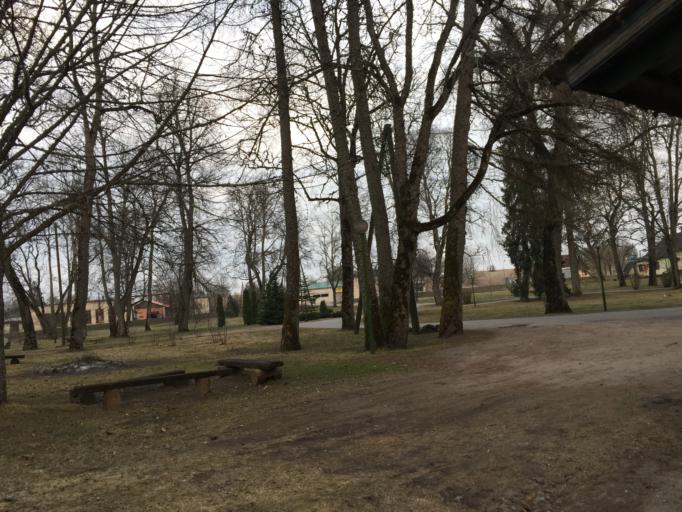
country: LV
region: Raunas
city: Rauna
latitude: 57.1615
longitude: 25.6625
